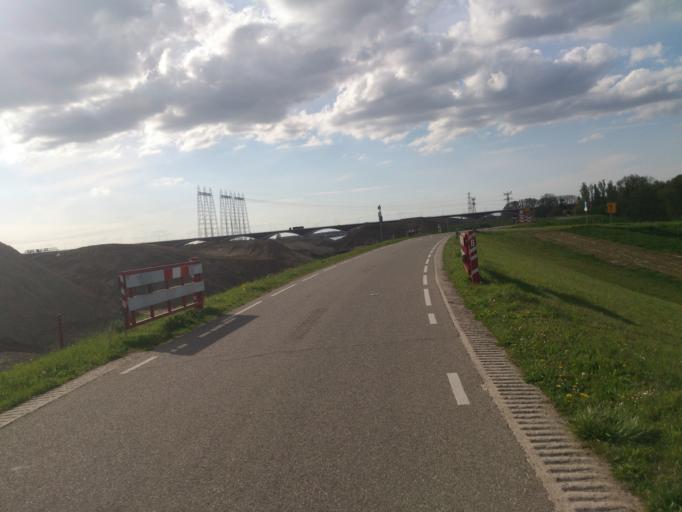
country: NL
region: Gelderland
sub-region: Gemeente Nijmegen
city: Nijmegen
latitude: 51.8599
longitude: 5.8531
